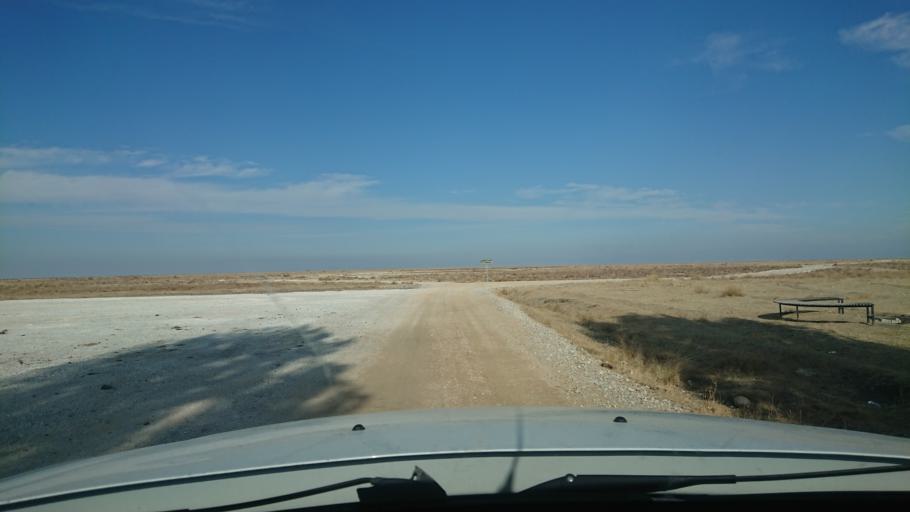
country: TR
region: Aksaray
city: Eskil
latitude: 38.4750
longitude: 33.4576
